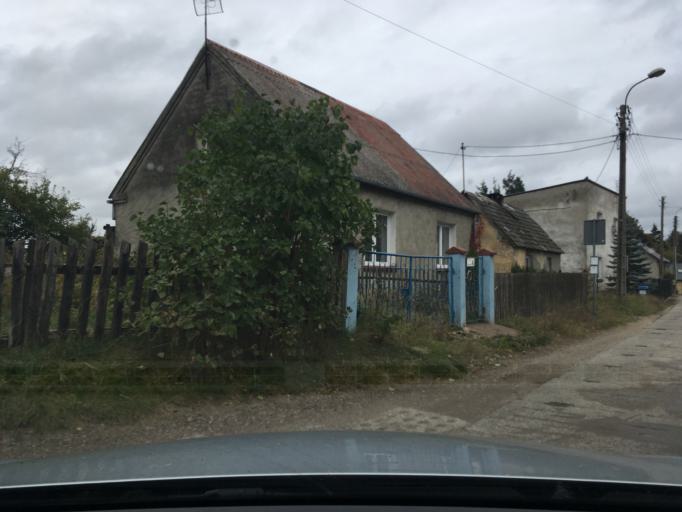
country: PL
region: Pomeranian Voivodeship
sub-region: Powiat koscierski
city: Koscierzyna
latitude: 54.1004
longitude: 17.9734
